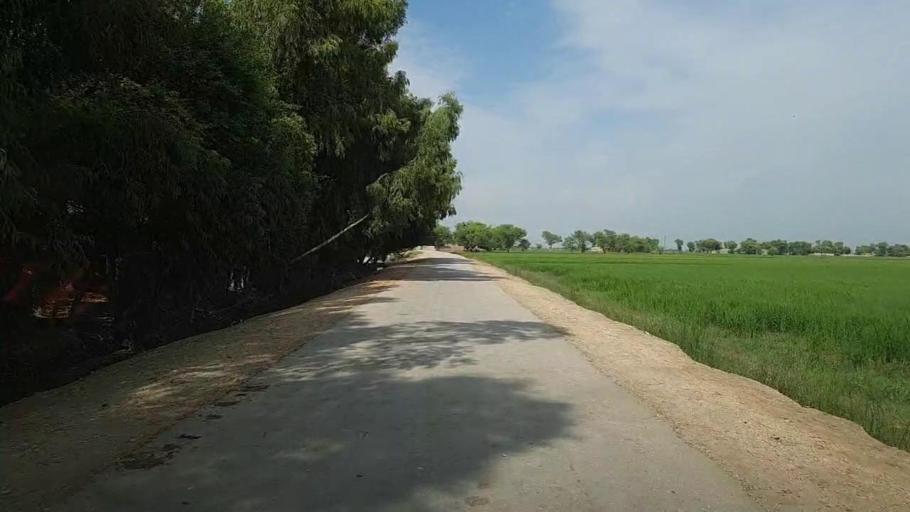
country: PK
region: Sindh
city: Thul
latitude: 28.2701
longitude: 68.8194
